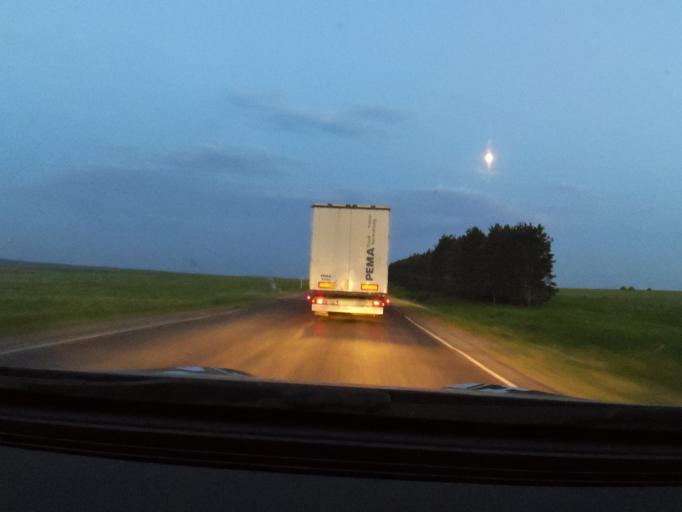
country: RU
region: Bashkortostan
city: Duvan
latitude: 56.0440
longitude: 58.2047
